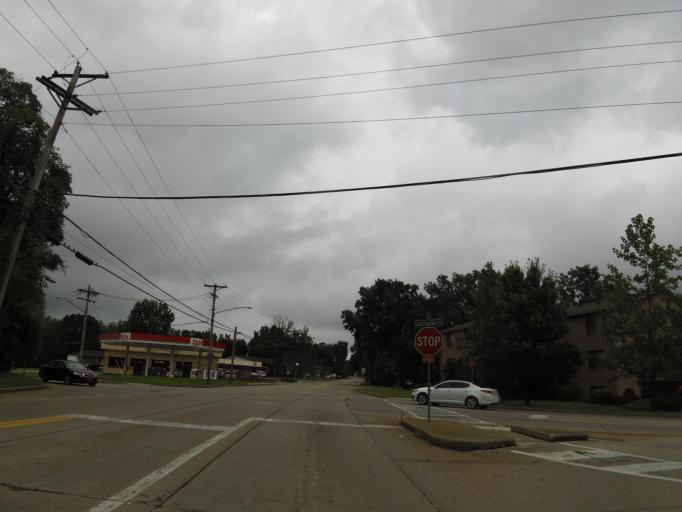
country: US
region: Missouri
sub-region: Cape Girardeau County
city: Cape Girardeau
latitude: 37.3379
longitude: -89.5530
